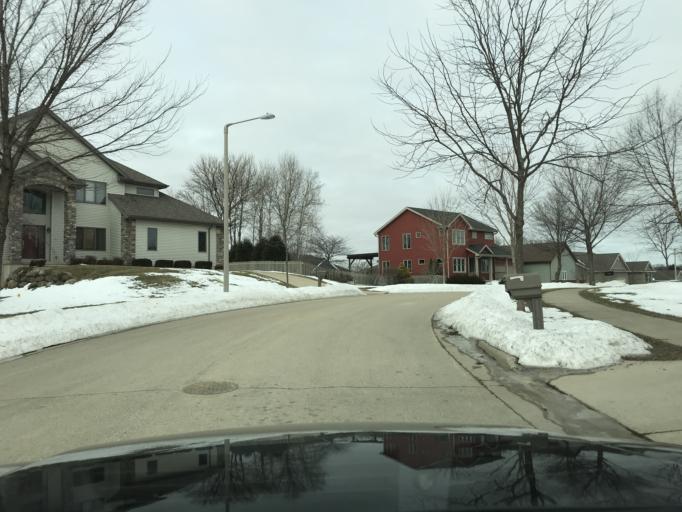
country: US
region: Wisconsin
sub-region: Dane County
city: Monona
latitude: 43.0952
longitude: -89.2709
